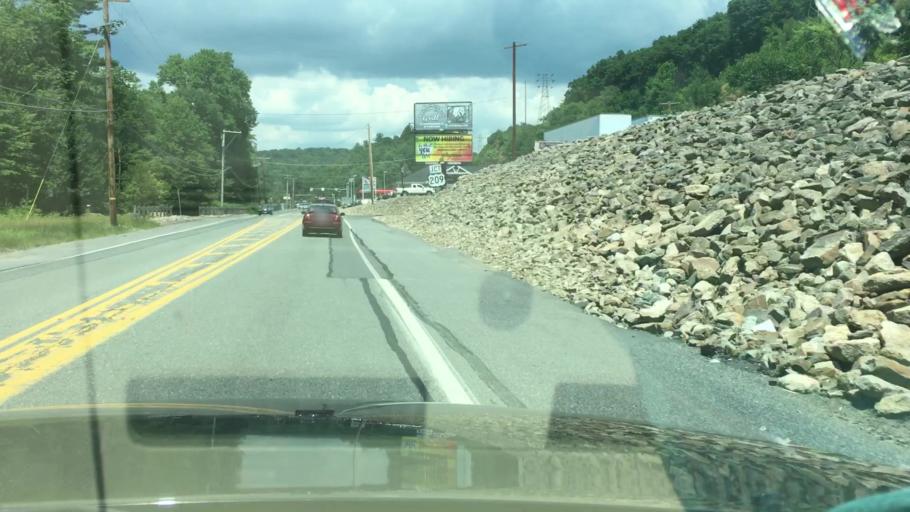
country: US
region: Pennsylvania
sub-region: Schuylkill County
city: Minersville
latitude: 40.6690
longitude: -76.2358
